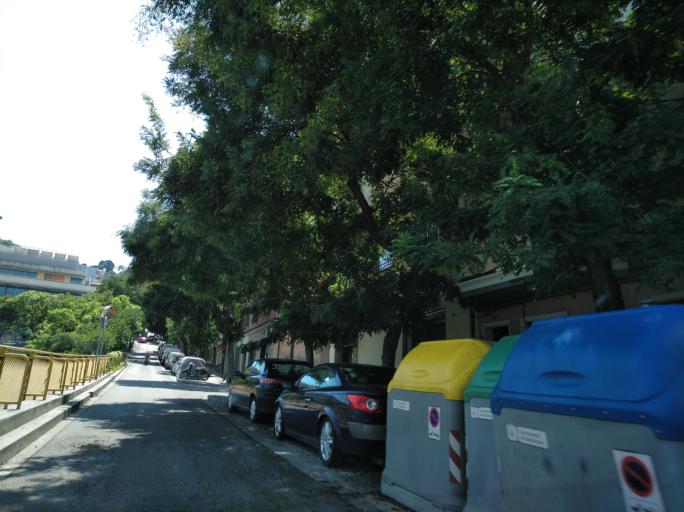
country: ES
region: Catalonia
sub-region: Provincia de Barcelona
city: Horta-Guinardo
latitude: 41.4243
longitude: 2.1579
